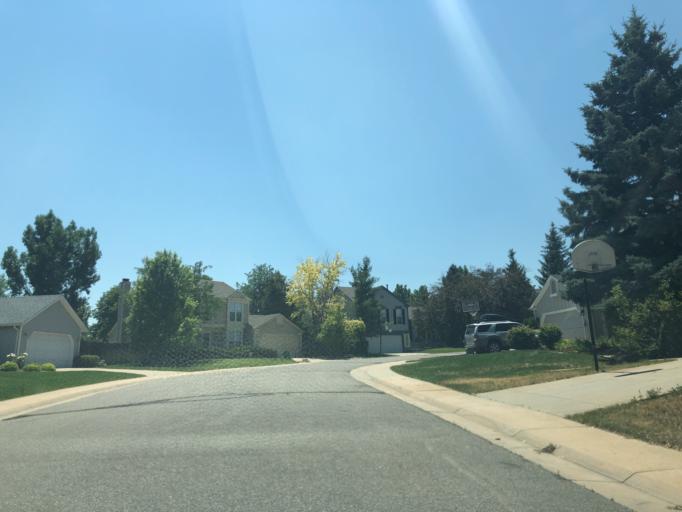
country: US
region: Colorado
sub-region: Arapahoe County
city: Dove Valley
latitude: 39.6192
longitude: -104.7547
